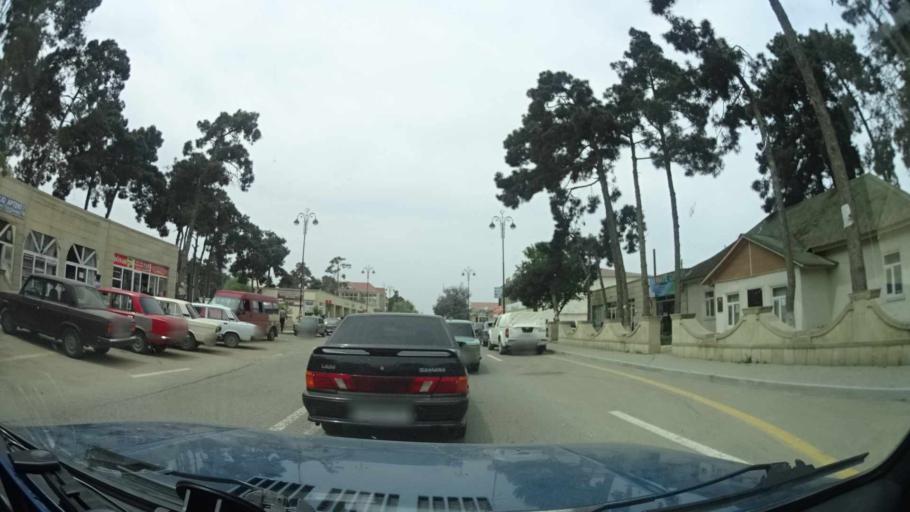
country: AZ
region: Bilasuvar Rayon
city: Pushkino
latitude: 39.4529
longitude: 48.5482
